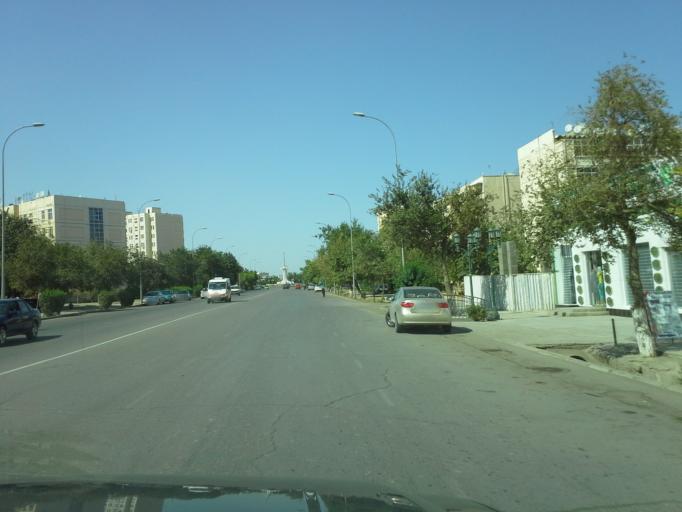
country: TM
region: Dasoguz
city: Dasoguz
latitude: 41.8301
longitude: 59.9728
